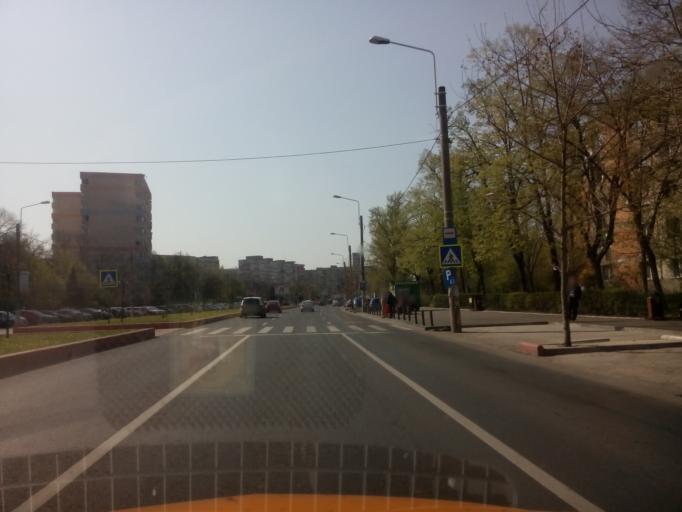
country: RO
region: Ilfov
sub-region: Comuna Popesti-Leordeni
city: Popesti-Leordeni
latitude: 44.4176
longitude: 26.1649
